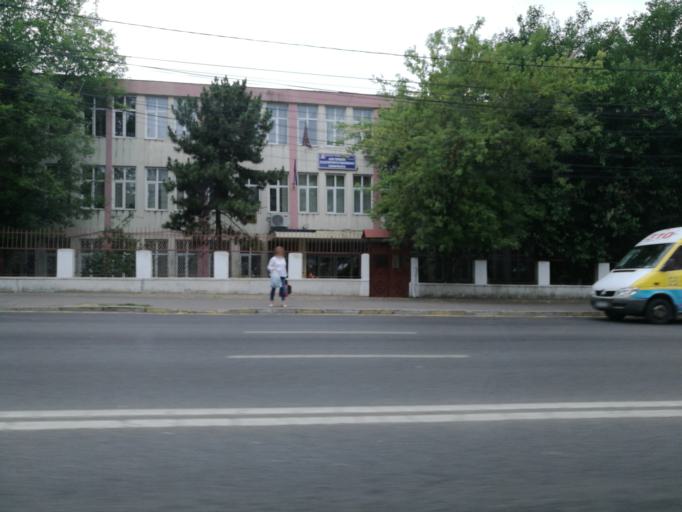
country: RO
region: Constanta
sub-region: Municipiul Constanta
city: Constanta
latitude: 44.1844
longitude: 28.6354
